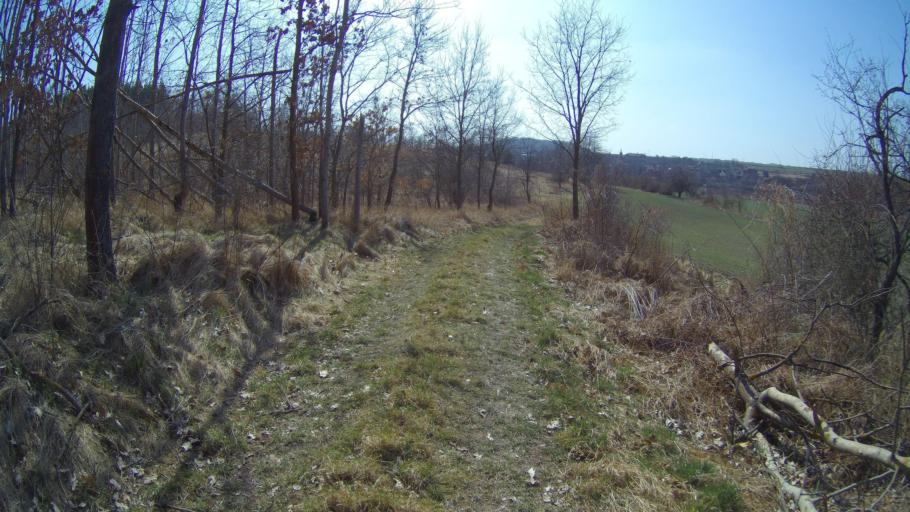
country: CZ
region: Ustecky
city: Mecholupy
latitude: 50.2867
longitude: 13.5673
